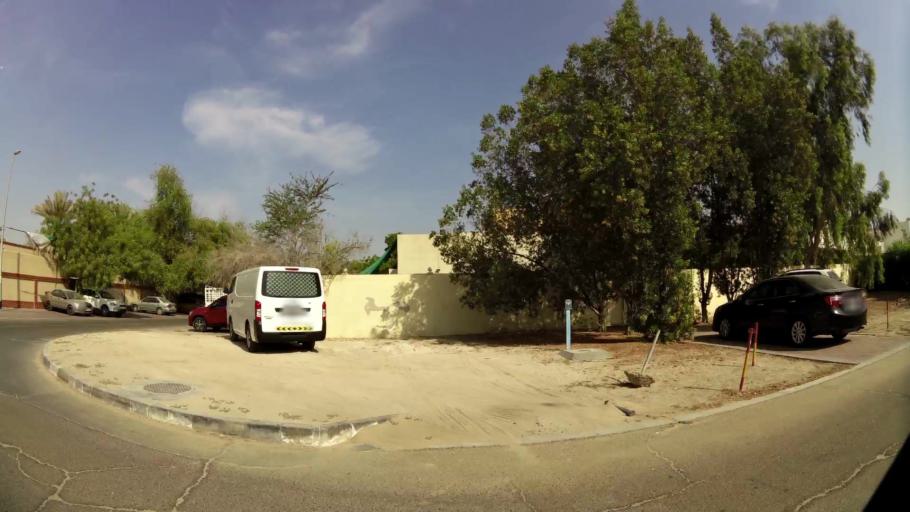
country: AE
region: Ash Shariqah
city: Sharjah
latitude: 25.2215
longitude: 55.3918
